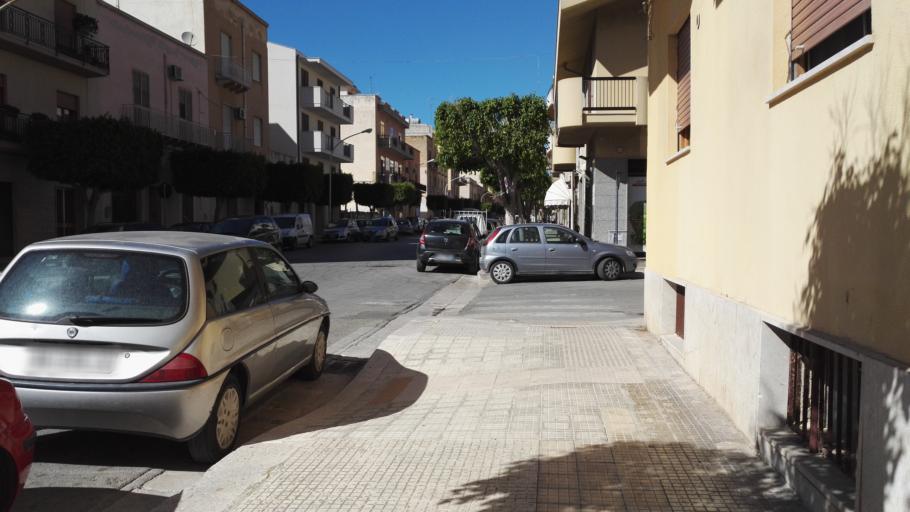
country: IT
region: Sicily
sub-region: Trapani
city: Marsala
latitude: 37.7941
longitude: 12.4361
